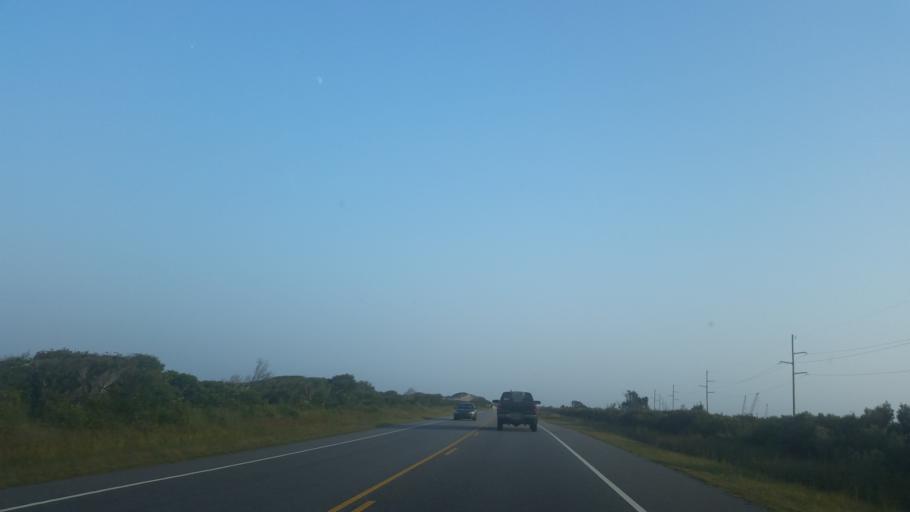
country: US
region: North Carolina
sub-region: Dare County
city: Wanchese
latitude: 35.8083
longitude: -75.5495
